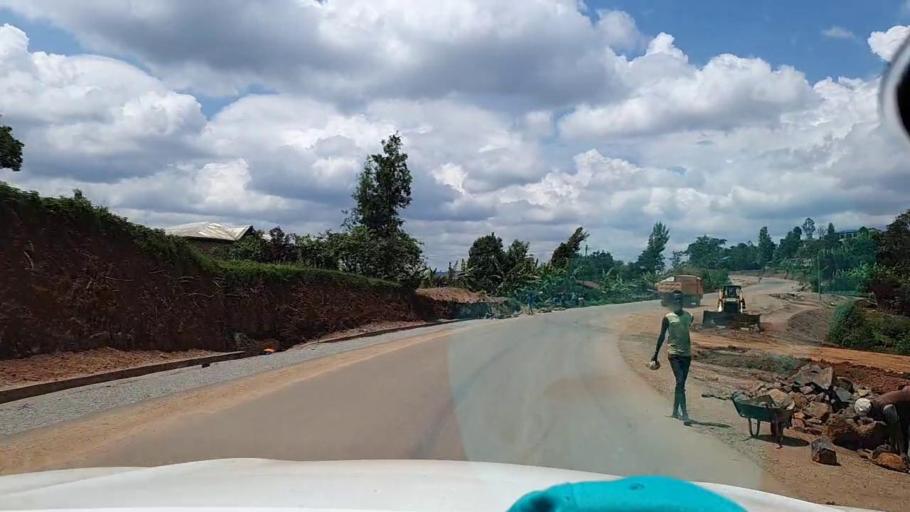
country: RW
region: Southern Province
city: Nzega
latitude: -2.6454
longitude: 29.5717
